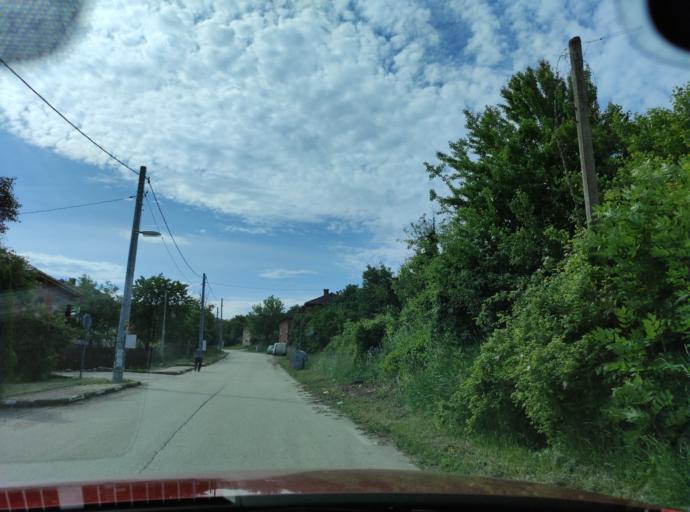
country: BG
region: Vidin
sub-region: Obshtina Belogradchik
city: Belogradchik
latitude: 43.5157
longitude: 22.7352
